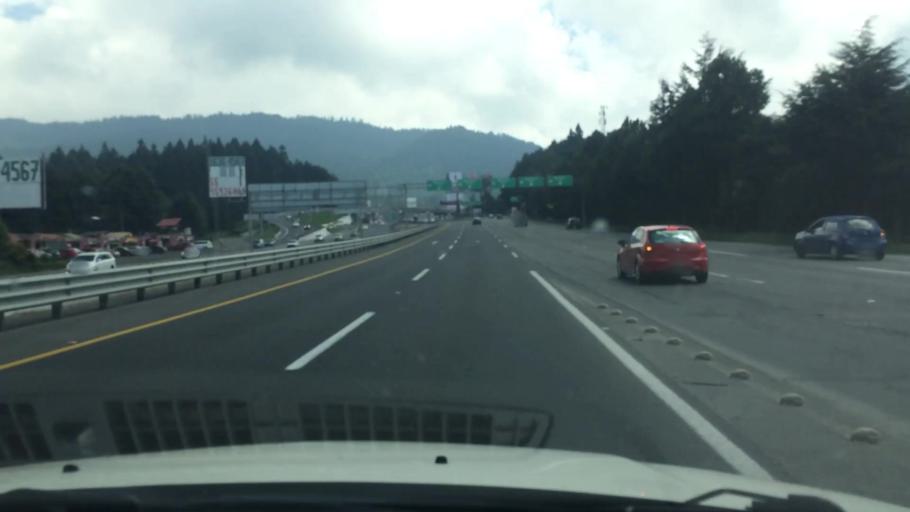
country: MX
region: Morelos
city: San Jeronimo Acazulco
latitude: 19.3005
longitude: -99.3801
